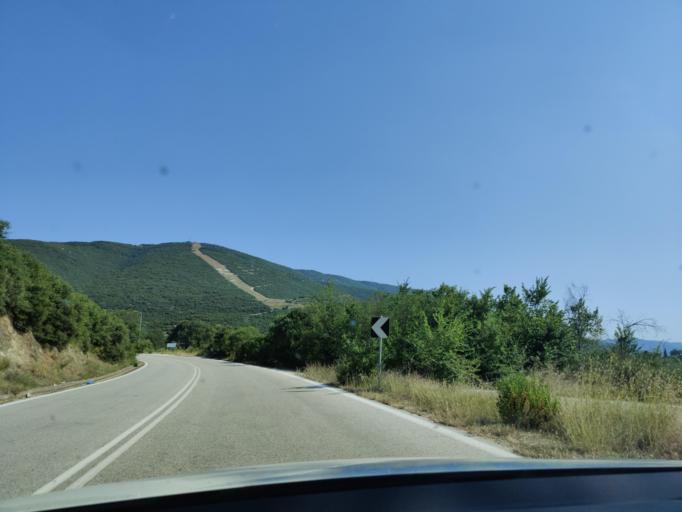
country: GR
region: East Macedonia and Thrace
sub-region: Nomos Kavalas
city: Zygos
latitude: 40.9986
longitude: 24.3805
